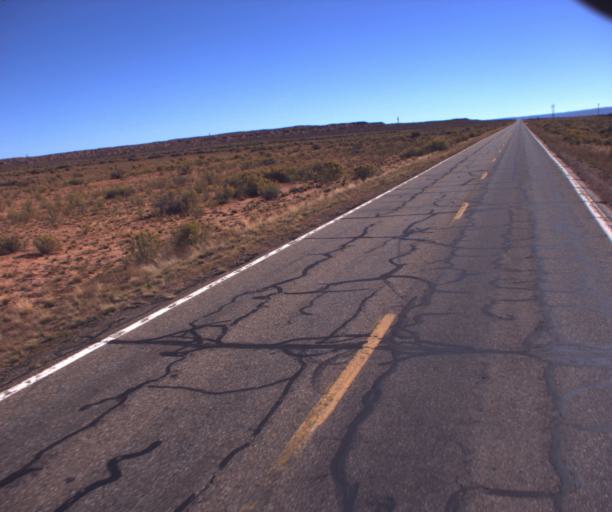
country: US
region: Arizona
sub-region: Coconino County
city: Fredonia
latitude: 36.9360
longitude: -112.5101
